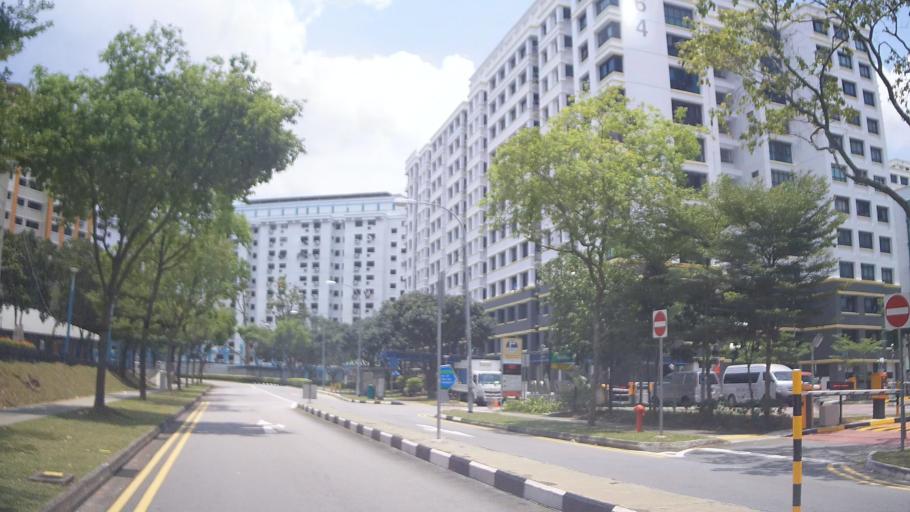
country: MY
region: Johor
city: Johor Bahru
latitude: 1.4447
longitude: 103.7974
